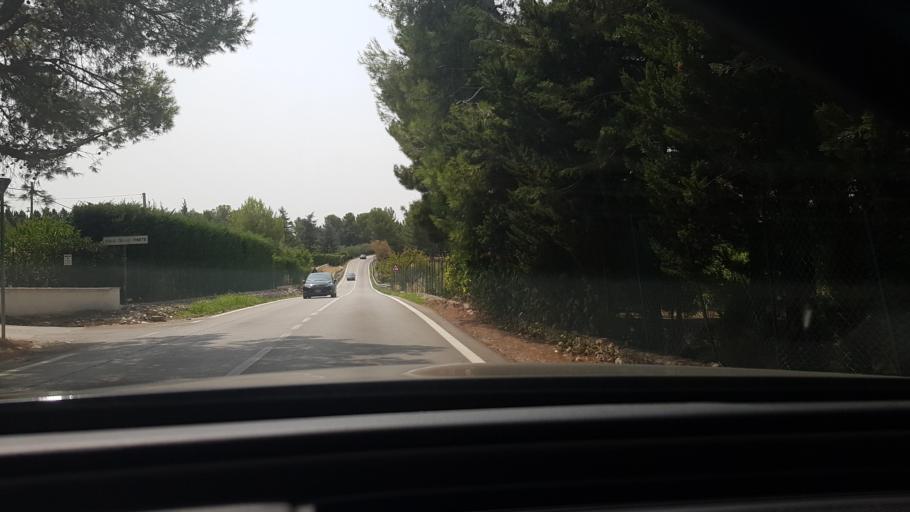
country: IT
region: Apulia
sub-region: Provincia di Barletta - Andria - Trani
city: Andria
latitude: 41.1256
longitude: 16.2875
